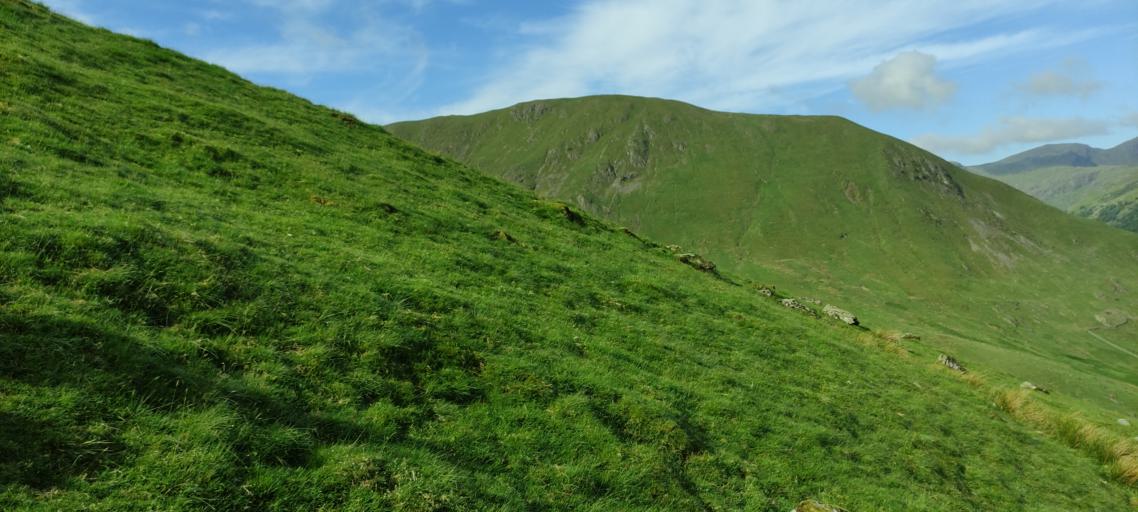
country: GB
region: England
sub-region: Cumbria
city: Ambleside
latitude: 54.5077
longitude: -2.8956
